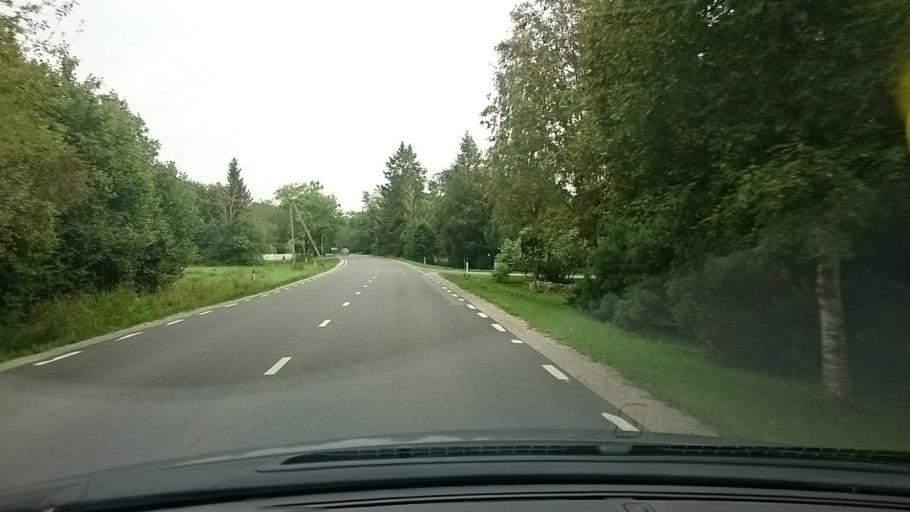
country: EE
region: Harju
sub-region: Harku vald
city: Tabasalu
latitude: 59.4269
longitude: 24.5272
